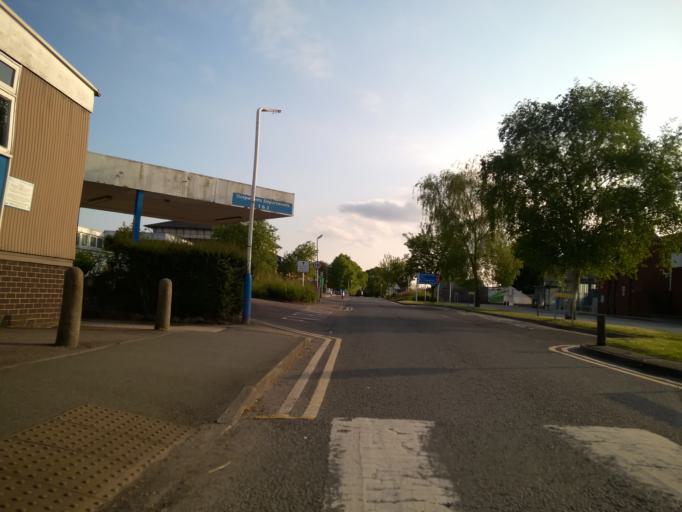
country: GB
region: England
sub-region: Leicestershire
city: Oadby
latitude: 52.6308
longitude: -1.0827
